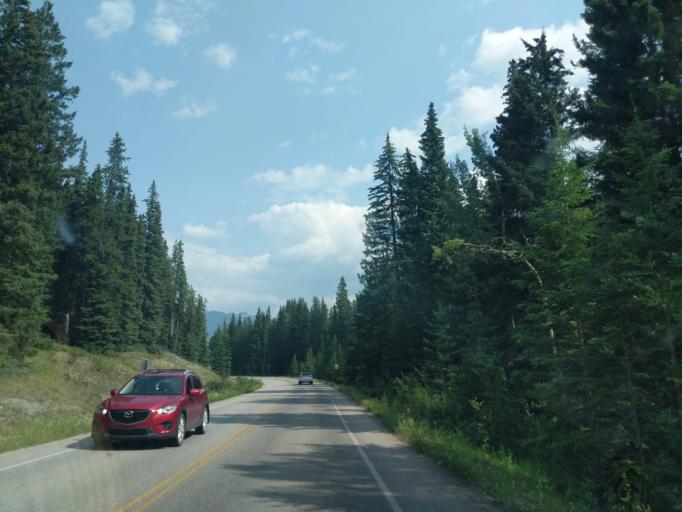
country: CA
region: Alberta
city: Banff
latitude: 51.1685
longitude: -115.6943
